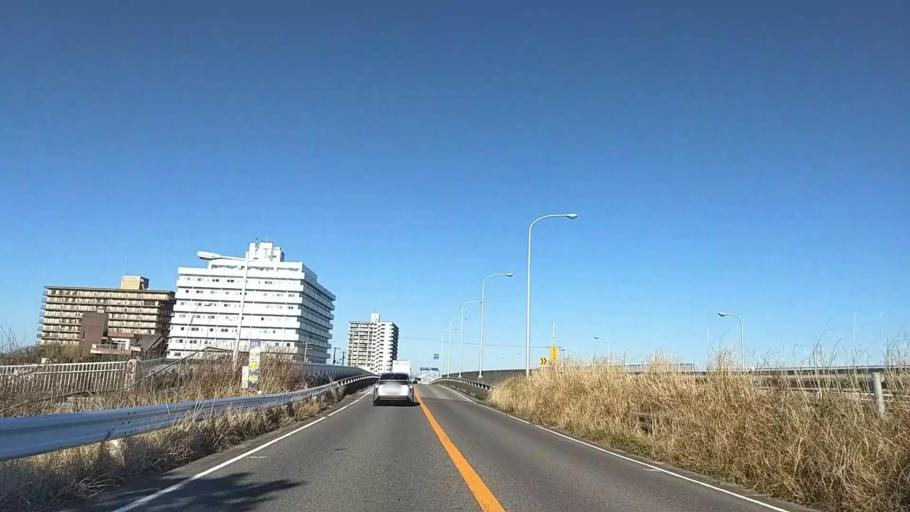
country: JP
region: Chiba
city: Mobara
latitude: 35.4488
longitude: 140.4022
